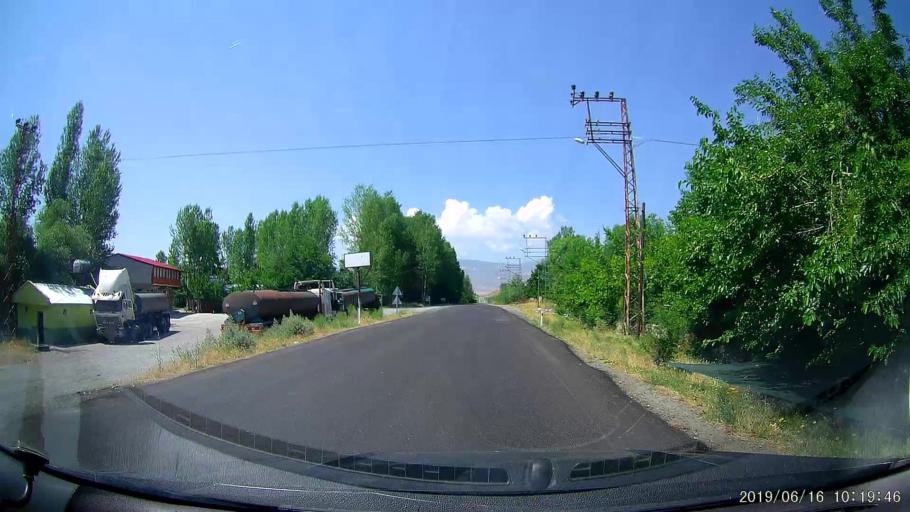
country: TR
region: Igdir
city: Tuzluca
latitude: 40.1529
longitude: 43.6536
